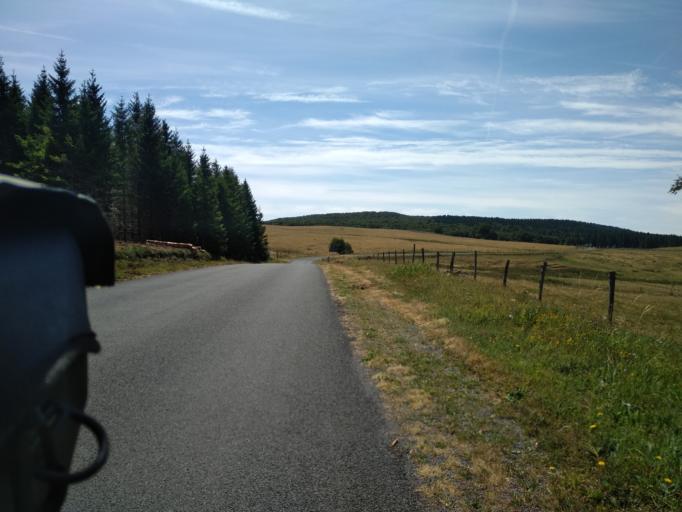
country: FR
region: Midi-Pyrenees
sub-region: Departement de l'Aveyron
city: Laguiole
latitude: 44.6609
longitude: 2.9584
